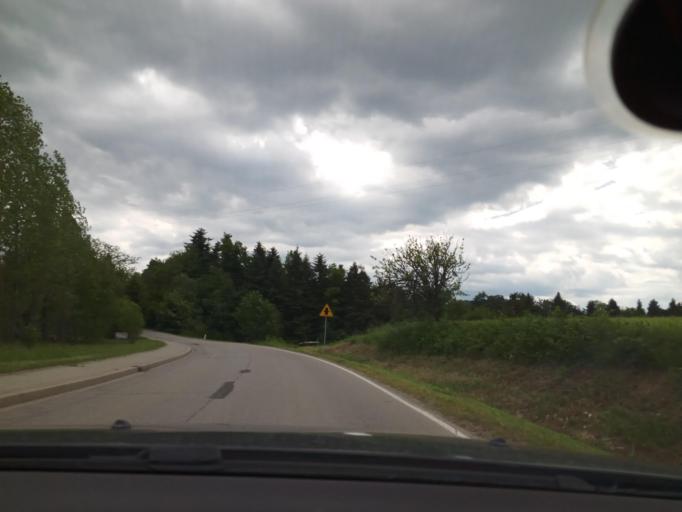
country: PL
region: Lesser Poland Voivodeship
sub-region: Powiat limanowski
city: Tymbark
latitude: 49.7954
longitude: 20.3206
